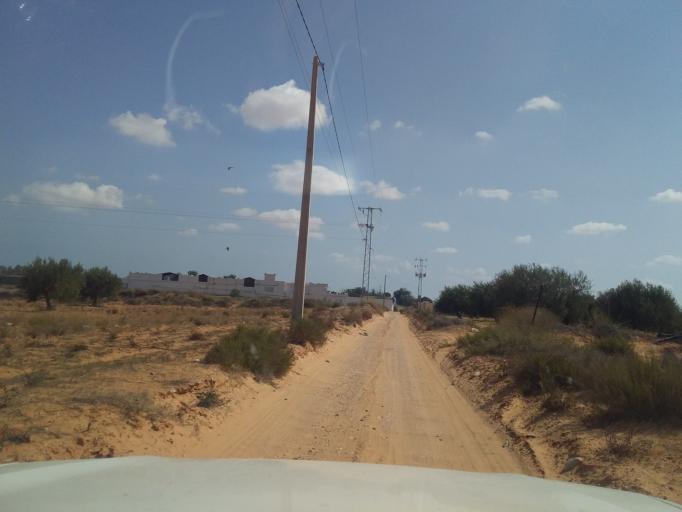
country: TN
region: Madanin
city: Medenine
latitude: 33.6005
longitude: 10.3146
